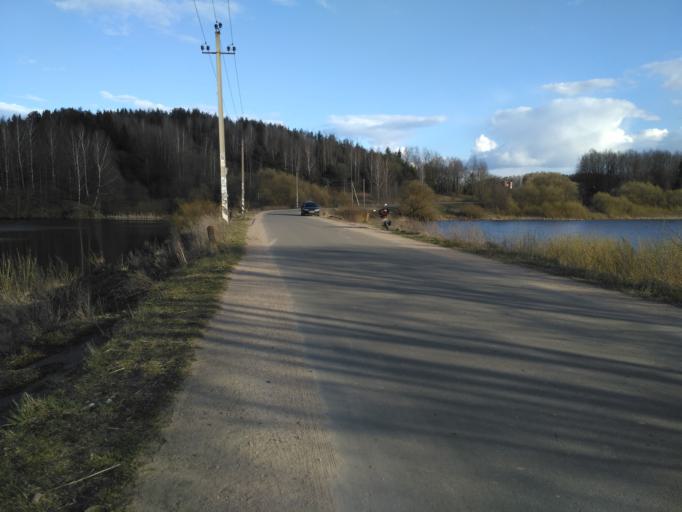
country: BY
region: Minsk
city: Lahoysk
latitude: 54.1008
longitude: 27.8174
